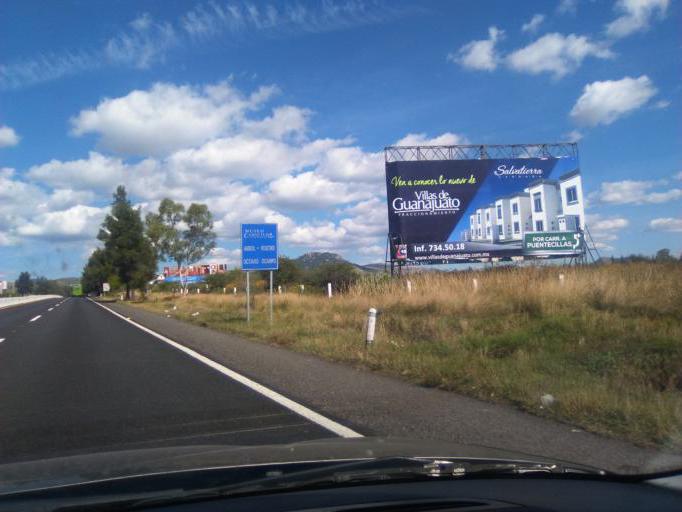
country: MX
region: Guanajuato
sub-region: Guanajuato
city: San Jose de Cervera
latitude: 20.9706
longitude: -101.3078
